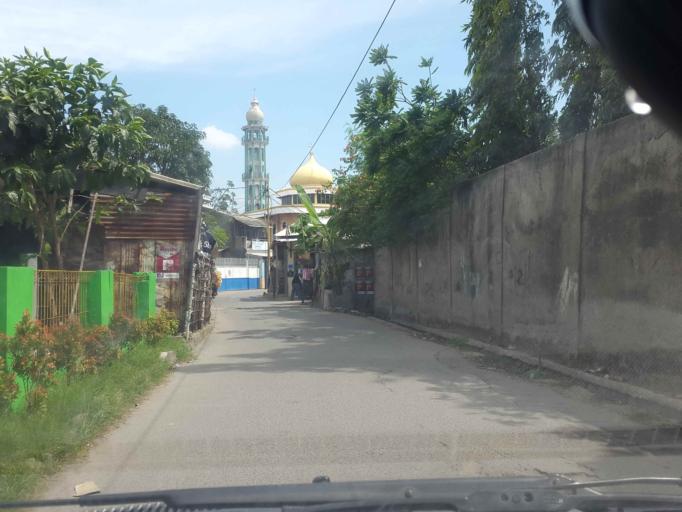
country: ID
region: Banten
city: Tangerang
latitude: -6.1502
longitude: 106.6802
